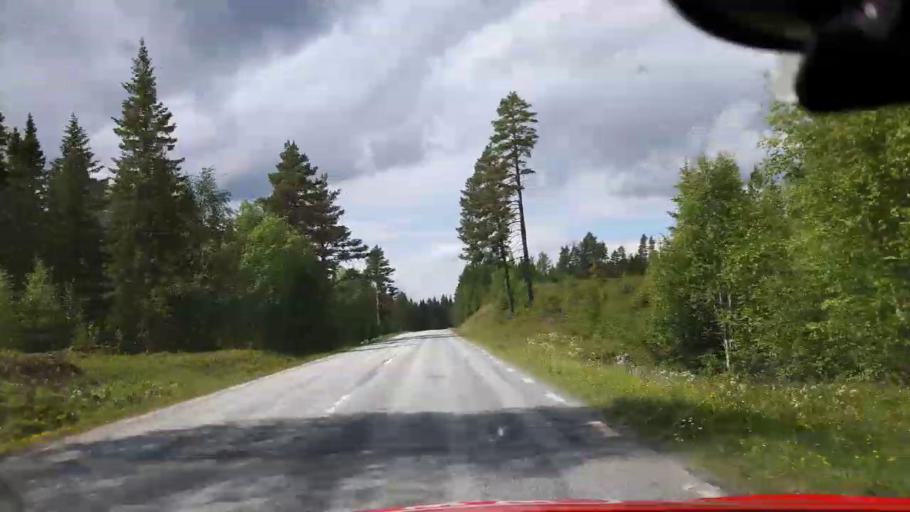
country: SE
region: Jaemtland
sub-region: Krokoms Kommun
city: Krokom
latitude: 63.4041
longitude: 14.2813
